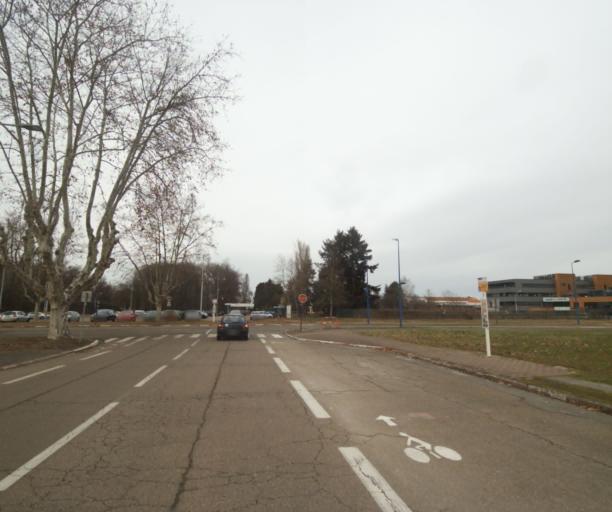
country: FR
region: Rhone-Alpes
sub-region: Departement de la Loire
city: Mably
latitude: 46.0666
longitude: 4.0822
